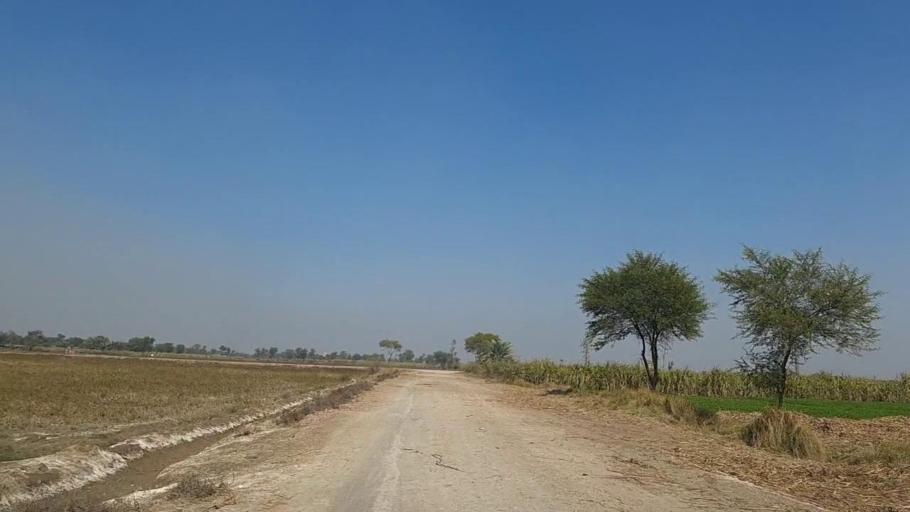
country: PK
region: Sindh
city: Daur
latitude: 26.4810
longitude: 68.3253
